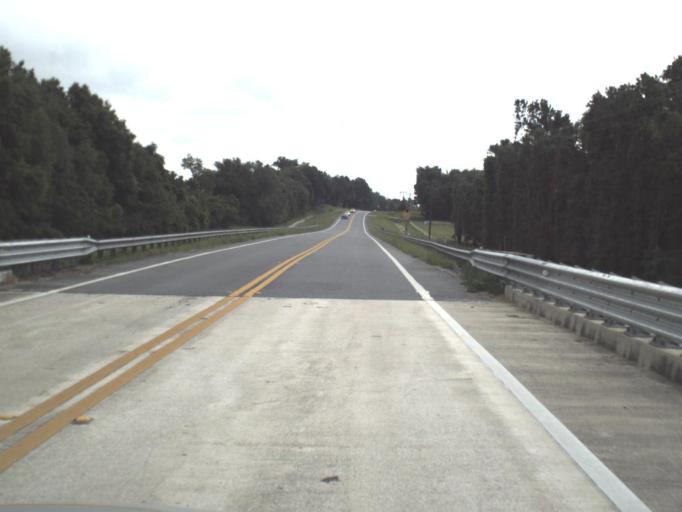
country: US
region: Florida
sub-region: Union County
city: Lake Butler
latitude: 29.8788
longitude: -82.3362
